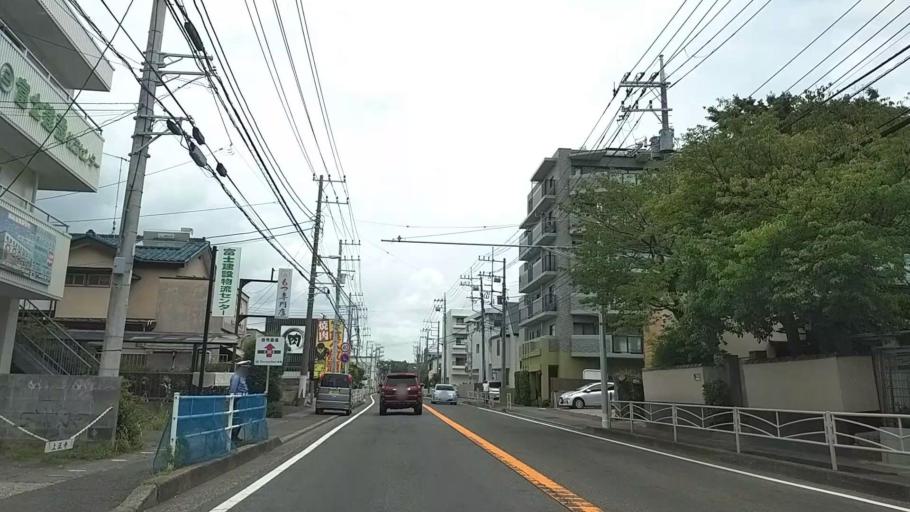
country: JP
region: Kanagawa
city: Chigasaki
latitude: 35.3398
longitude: 139.4356
